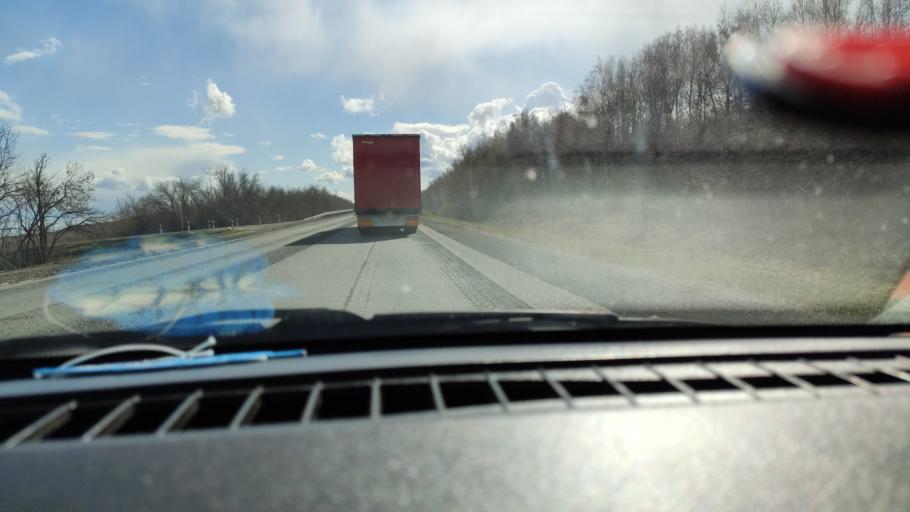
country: RU
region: Saratov
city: Dukhovnitskoye
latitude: 52.6360
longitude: 48.1880
